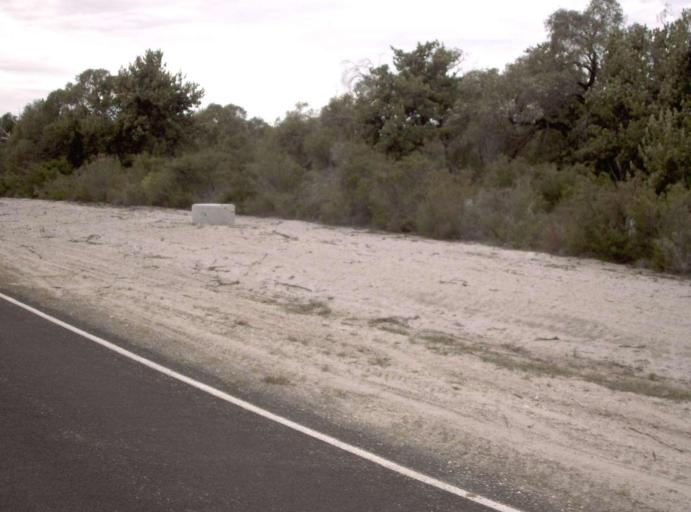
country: AU
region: Victoria
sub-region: Wellington
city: Sale
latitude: -38.1745
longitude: 147.3818
